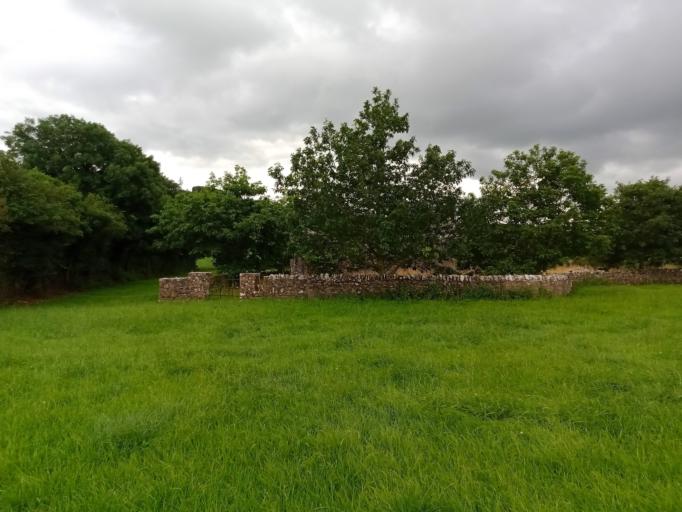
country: IE
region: Leinster
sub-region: Laois
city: Stradbally
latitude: 52.9579
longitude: -7.1901
